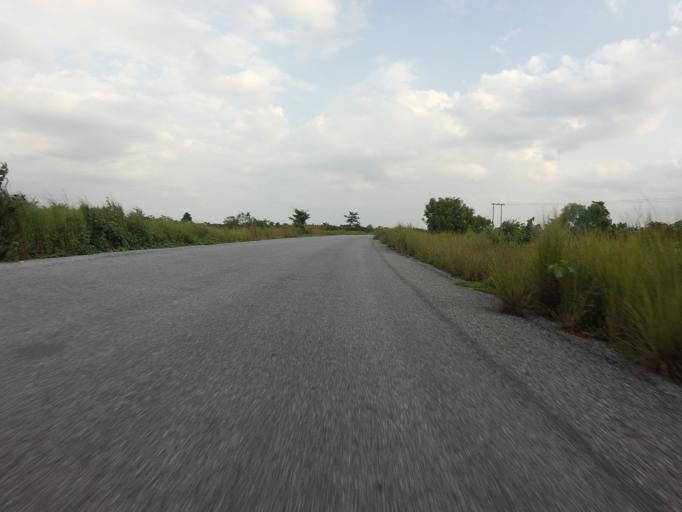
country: GH
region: Volta
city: Ho
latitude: 6.3814
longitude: 0.5315
